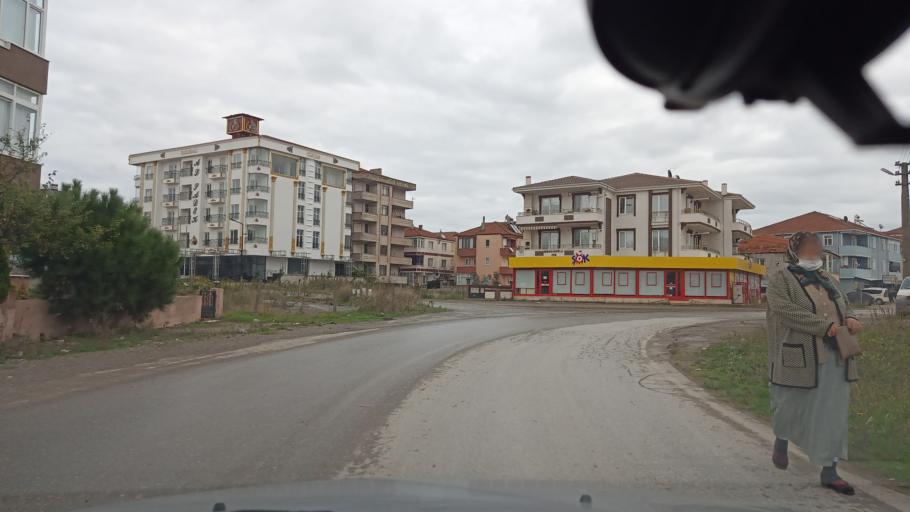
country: TR
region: Sakarya
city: Karasu
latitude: 41.1088
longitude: 30.6879
